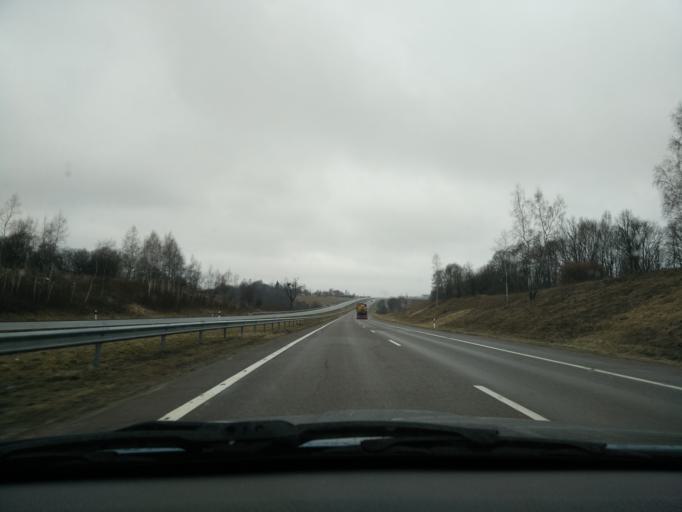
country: LT
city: Silale
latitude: 55.5162
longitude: 22.3790
